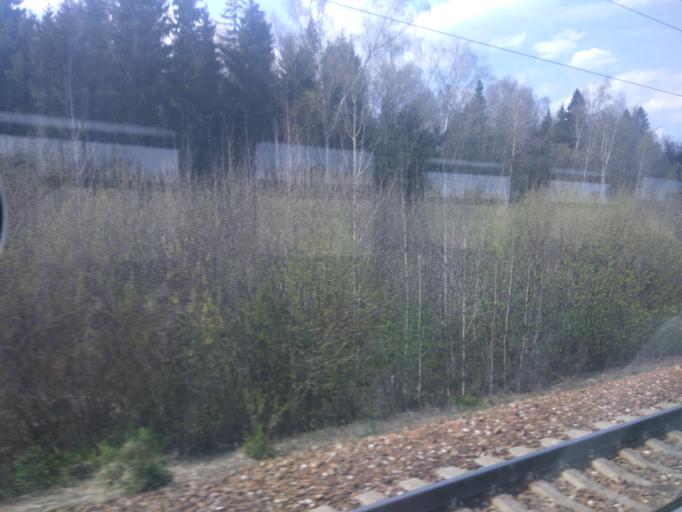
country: RU
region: Moskovskaya
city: Podosinki
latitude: 56.2181
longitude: 37.5271
